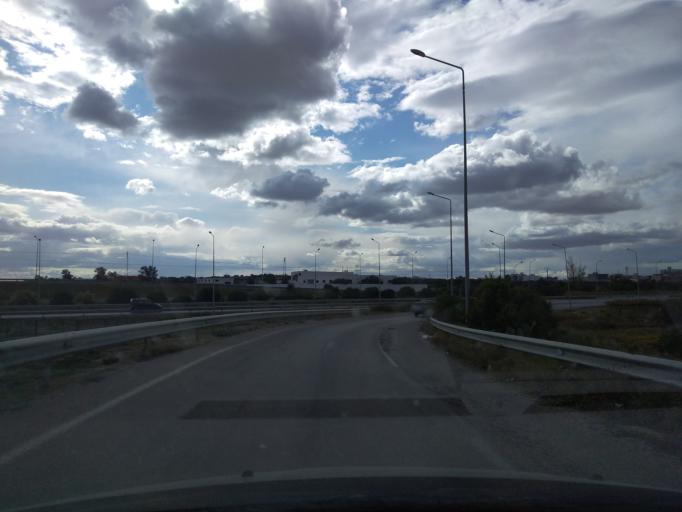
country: TN
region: Susah
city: Masakin
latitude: 35.7128
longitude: 10.5589
